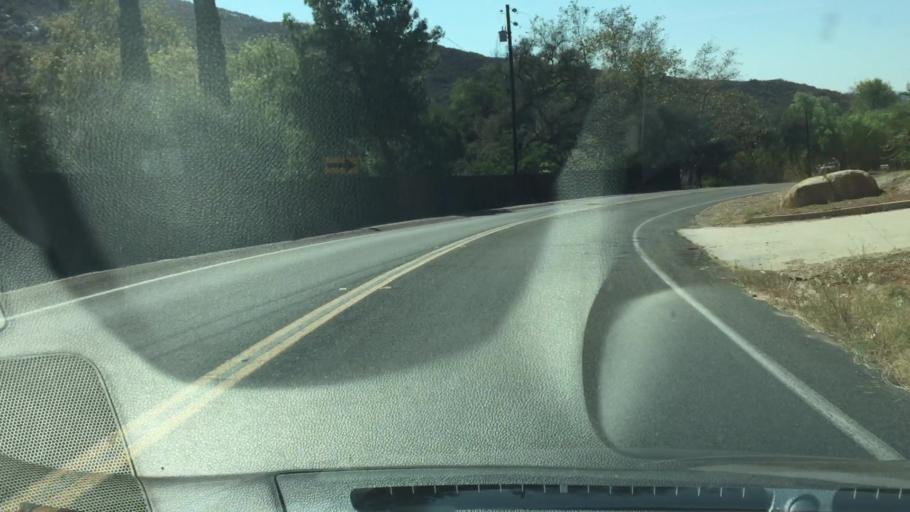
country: US
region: California
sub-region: San Diego County
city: Jamul
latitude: 32.7348
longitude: -116.8904
